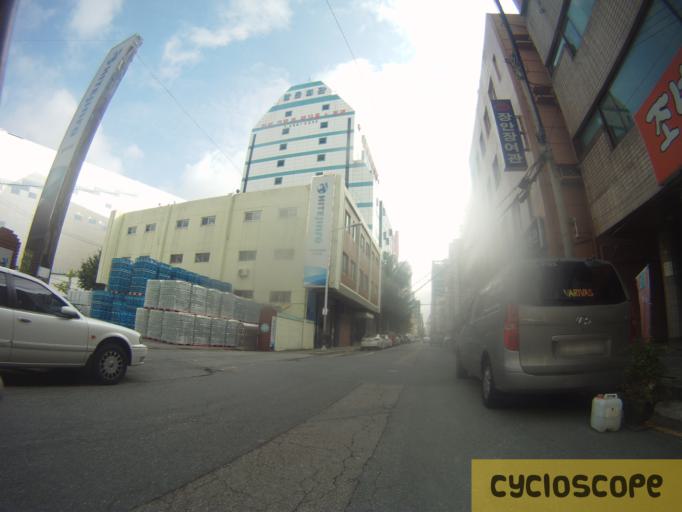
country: KR
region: Busan
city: Busan
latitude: 35.1182
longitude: 129.0421
